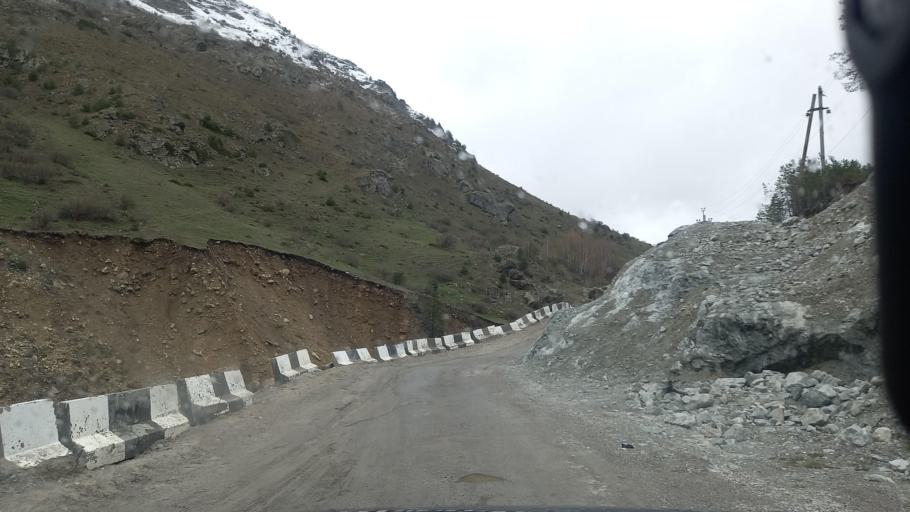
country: RU
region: Kabardino-Balkariya
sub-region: El'brusskiy Rayon
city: El'brus
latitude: 43.2288
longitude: 42.6565
